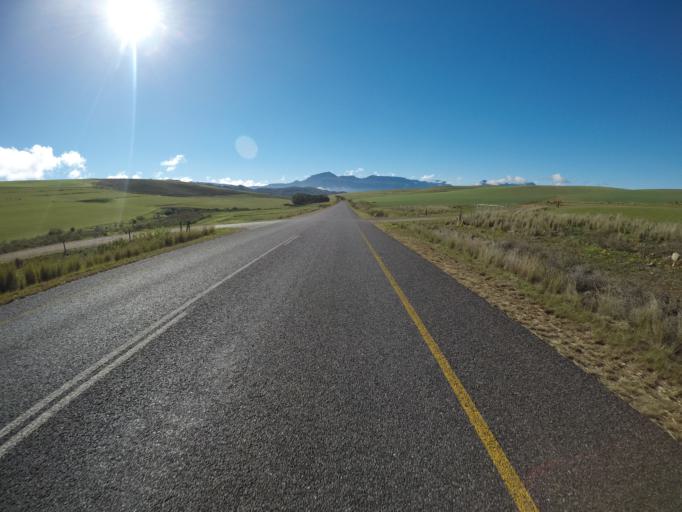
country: ZA
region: Western Cape
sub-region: Overberg District Municipality
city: Caledon
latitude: -34.1196
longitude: 19.5186
